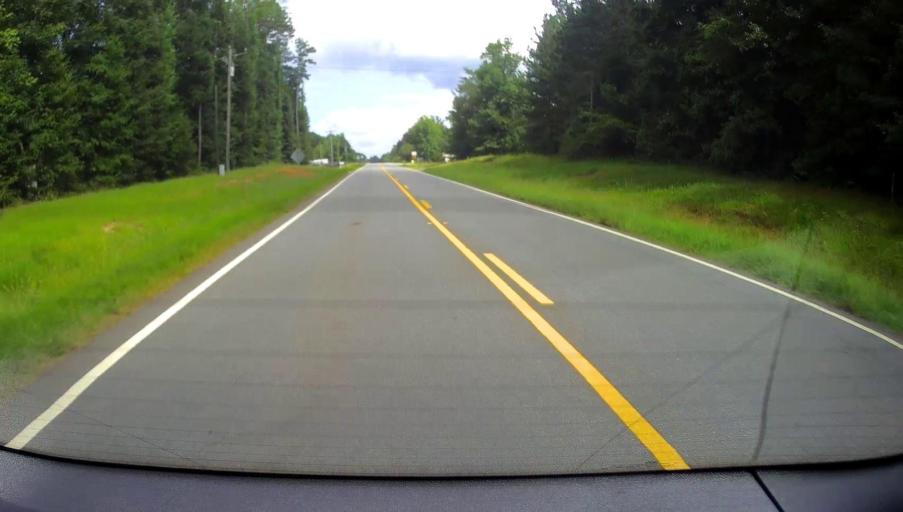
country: US
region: Georgia
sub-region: Bibb County
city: West Point
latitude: 32.8648
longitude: -83.8665
